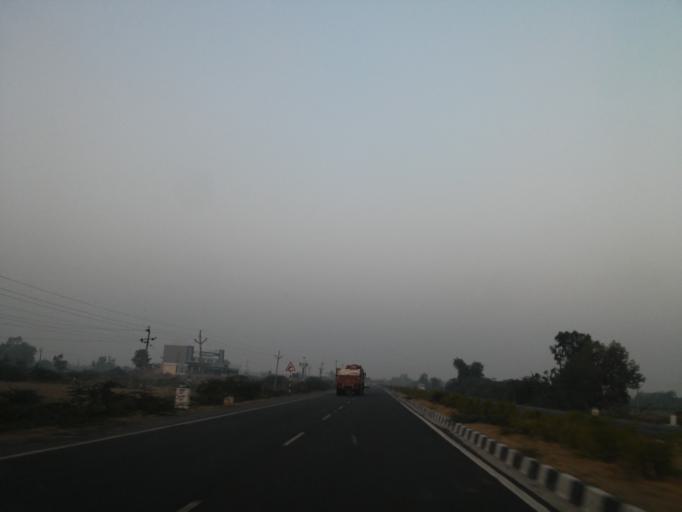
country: IN
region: Gujarat
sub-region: Surendranagar
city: Dhrangadhra
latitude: 23.0001
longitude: 71.3572
